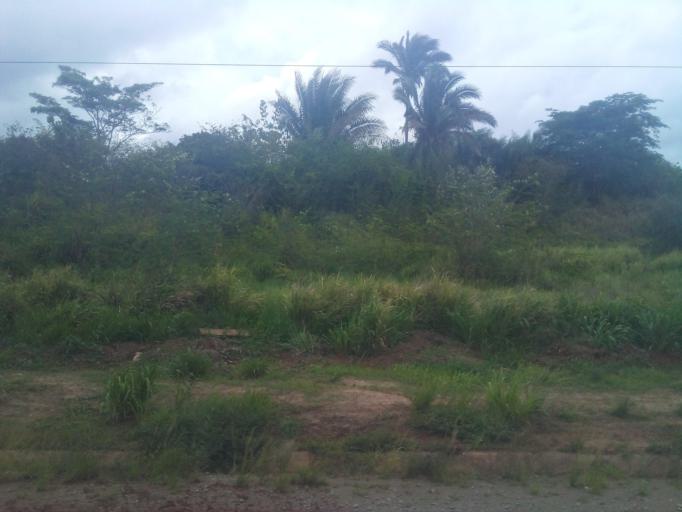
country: BR
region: Maranhao
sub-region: Santa Ines
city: Santa Ines
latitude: -3.6880
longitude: -45.3541
